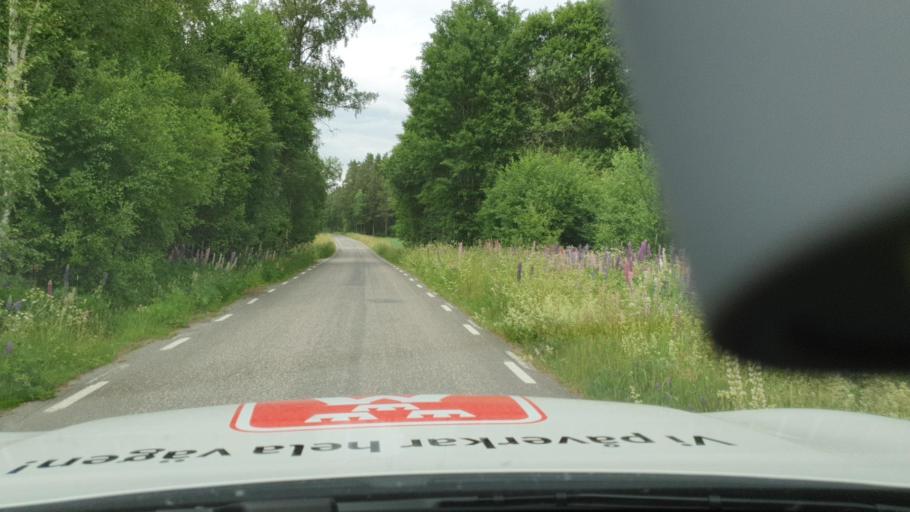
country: SE
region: Vaestra Goetaland
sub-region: Tidaholms Kommun
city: Tidaholm
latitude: 58.1710
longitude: 14.0142
